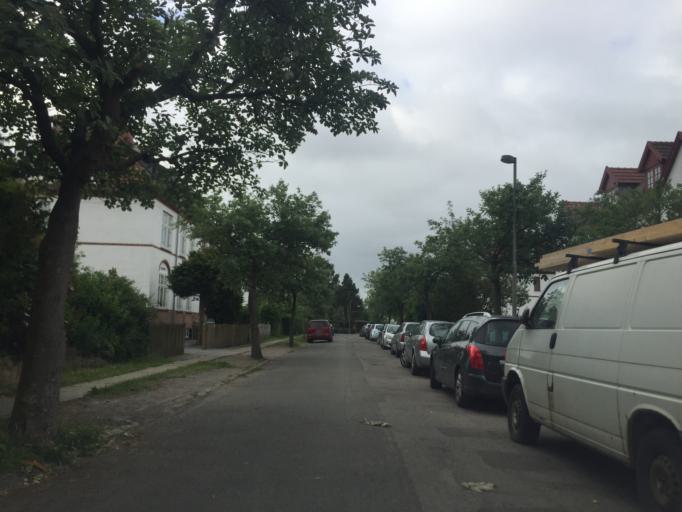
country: DK
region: Capital Region
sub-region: Kobenhavn
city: Vanlose
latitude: 55.6675
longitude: 12.4962
